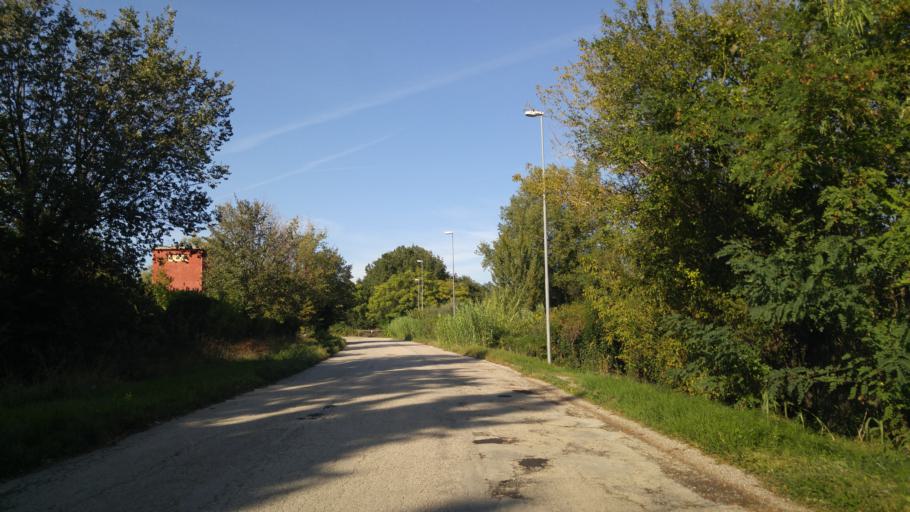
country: IT
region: The Marches
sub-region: Provincia di Pesaro e Urbino
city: Bellocchi
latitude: 43.8012
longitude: 13.0197
